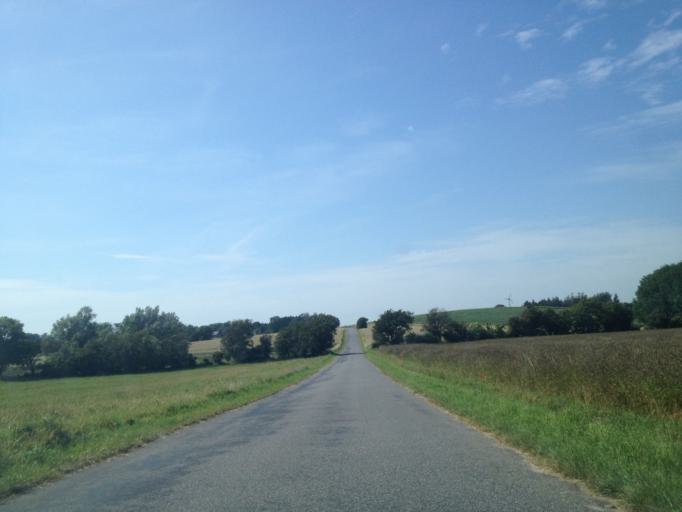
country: DK
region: Central Jutland
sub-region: Samso Kommune
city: Tranebjerg
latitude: 55.7969
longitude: 10.5680
